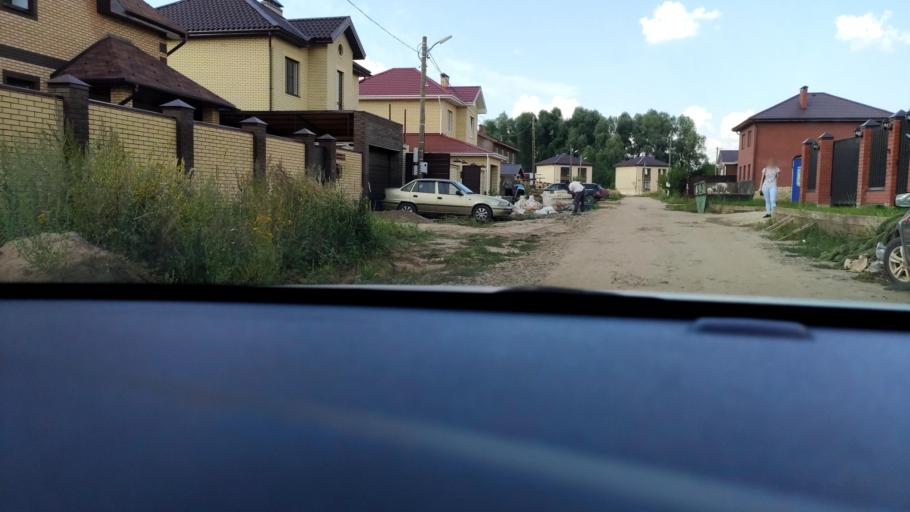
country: RU
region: Tatarstan
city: Vysokaya Gora
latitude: 55.7920
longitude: 49.2589
